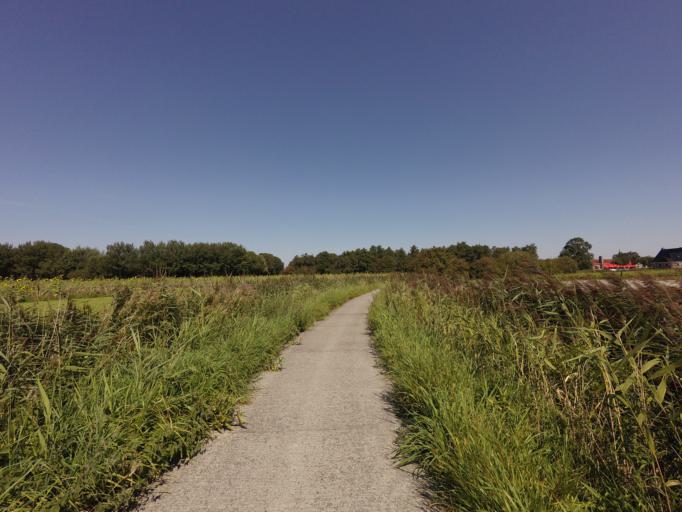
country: NL
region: Friesland
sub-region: Gemeente Dongeradeel
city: Anjum
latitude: 53.4002
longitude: 6.0803
